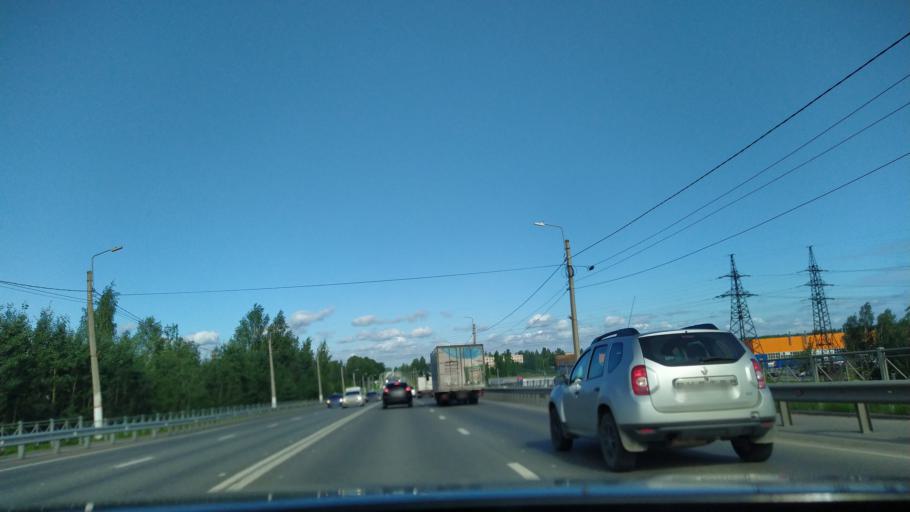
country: RU
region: Leningrad
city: Tosno
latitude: 59.5522
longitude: 30.8565
